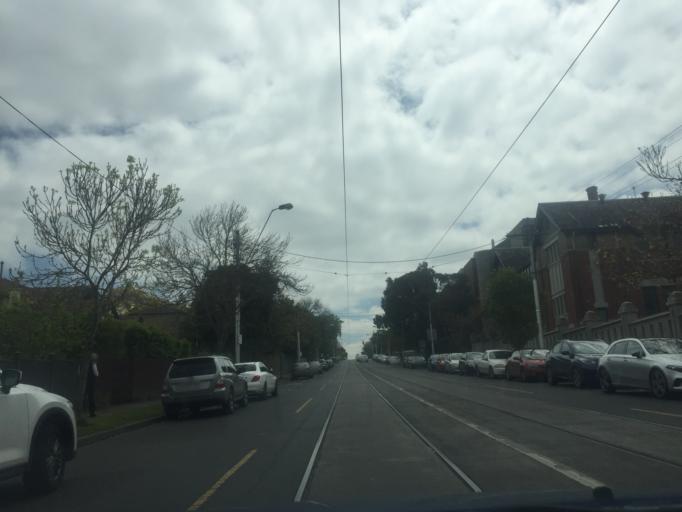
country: AU
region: Victoria
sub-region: Boroondara
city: Kew
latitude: -37.8141
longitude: 145.0369
